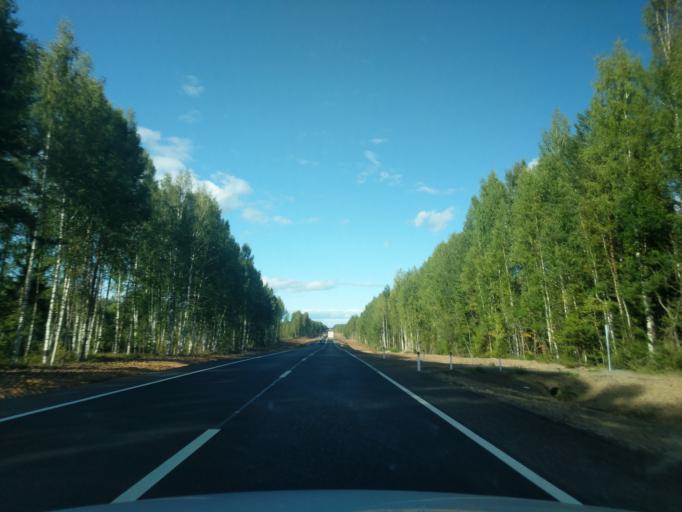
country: RU
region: Kostroma
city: Makar'yev
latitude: 57.9817
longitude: 43.9583
